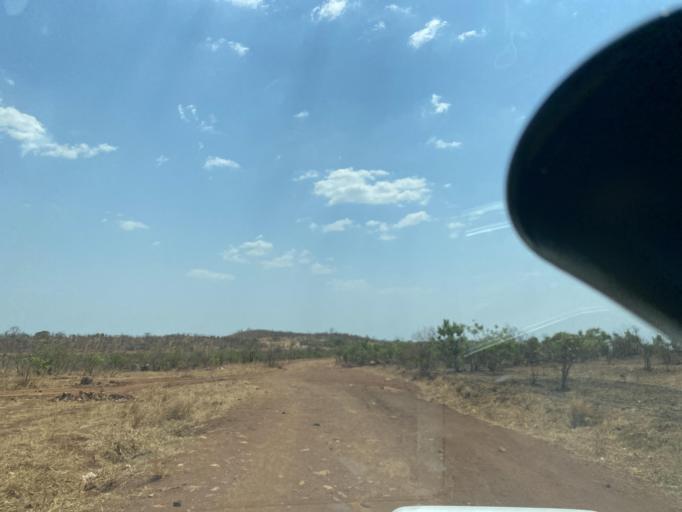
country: ZM
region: Lusaka
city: Lusaka
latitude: -15.4989
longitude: 27.9490
